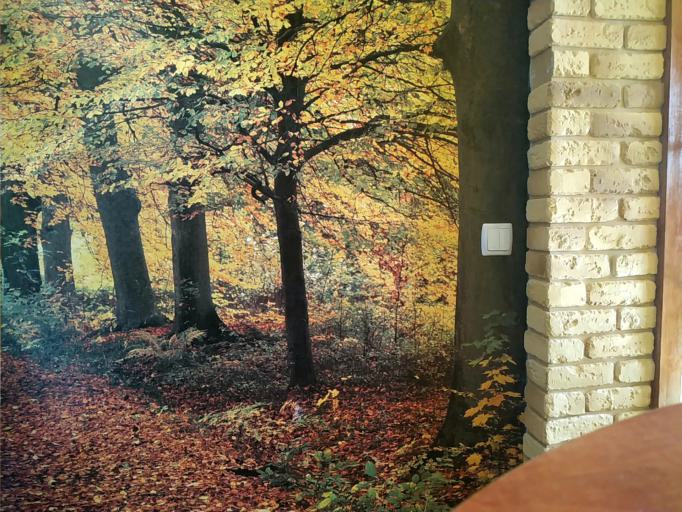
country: RU
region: Jaroslavl
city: Kukoboy
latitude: 58.8597
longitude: 39.7297
